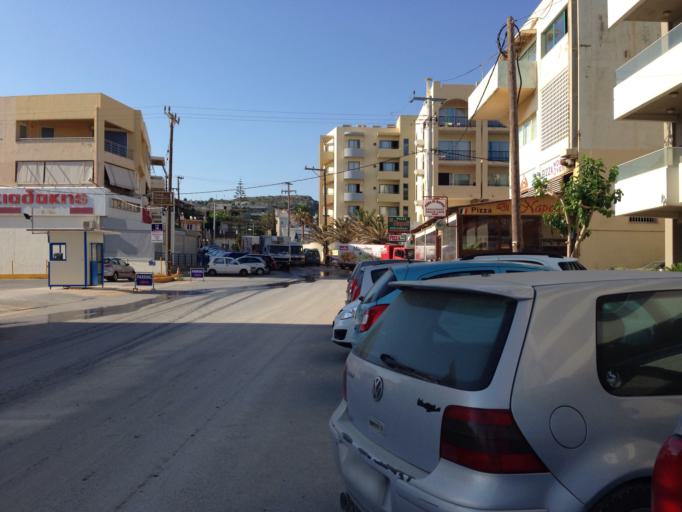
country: GR
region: Crete
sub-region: Nomos Rethymnis
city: Rethymno
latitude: 35.3669
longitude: 24.4915
